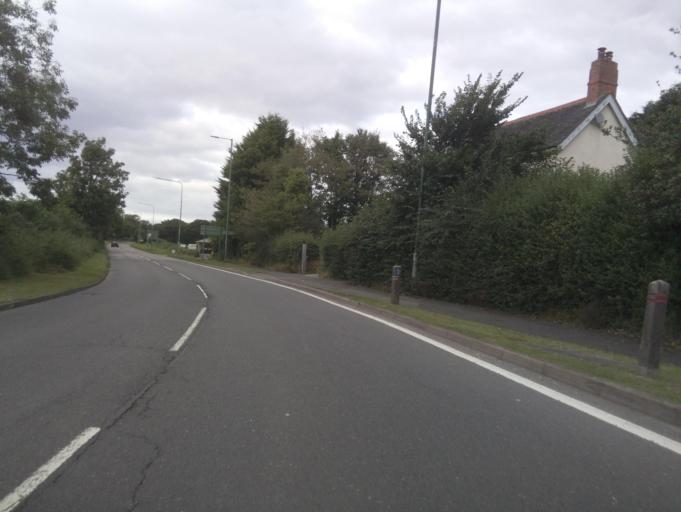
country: GB
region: England
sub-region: Solihull
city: Cheswick Green
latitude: 52.3650
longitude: -1.7821
